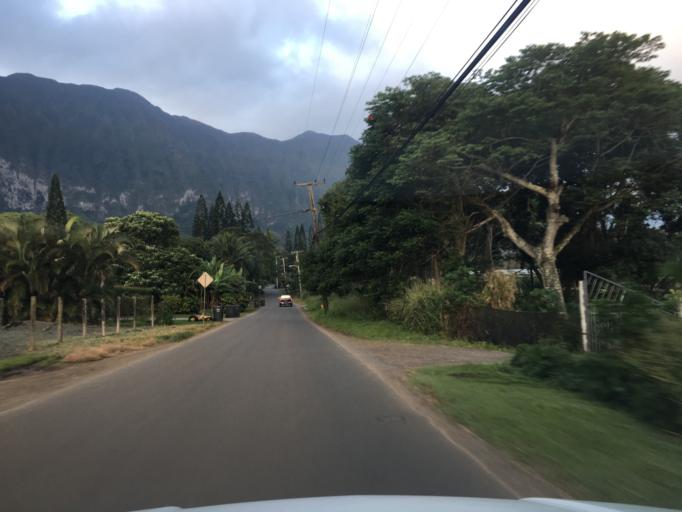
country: US
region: Hawaii
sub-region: Honolulu County
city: Waimanalo
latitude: 21.3402
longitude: -157.7345
